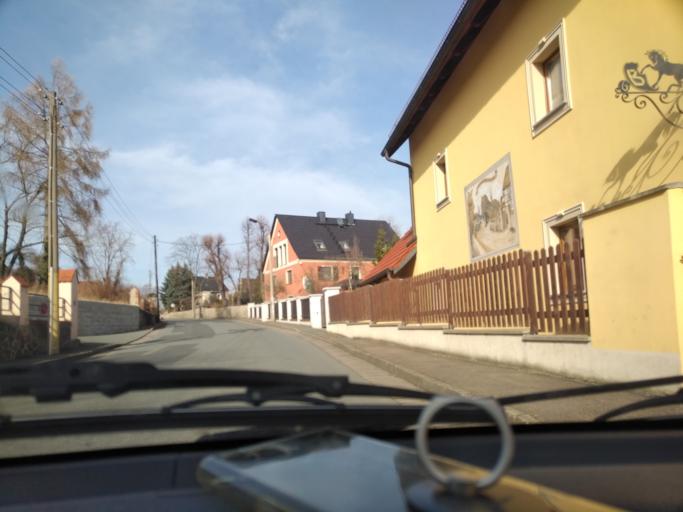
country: DE
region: Saxony
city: Glaubitz
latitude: 51.3187
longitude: 13.3809
